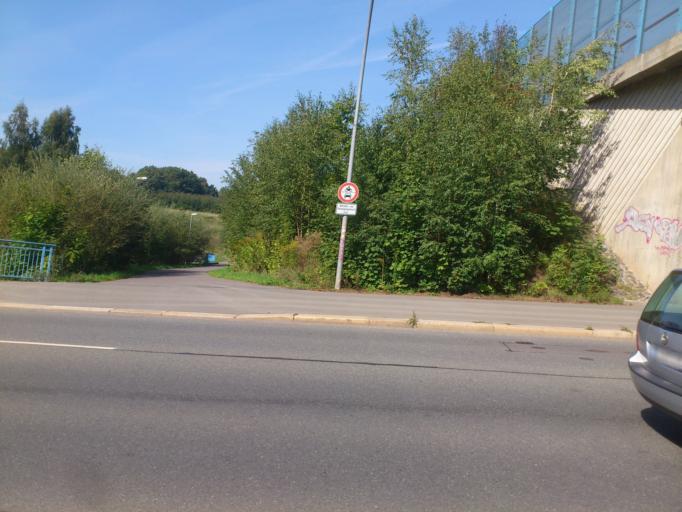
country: DE
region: Saxony
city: Neukirchen
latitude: 50.8188
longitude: 12.8558
